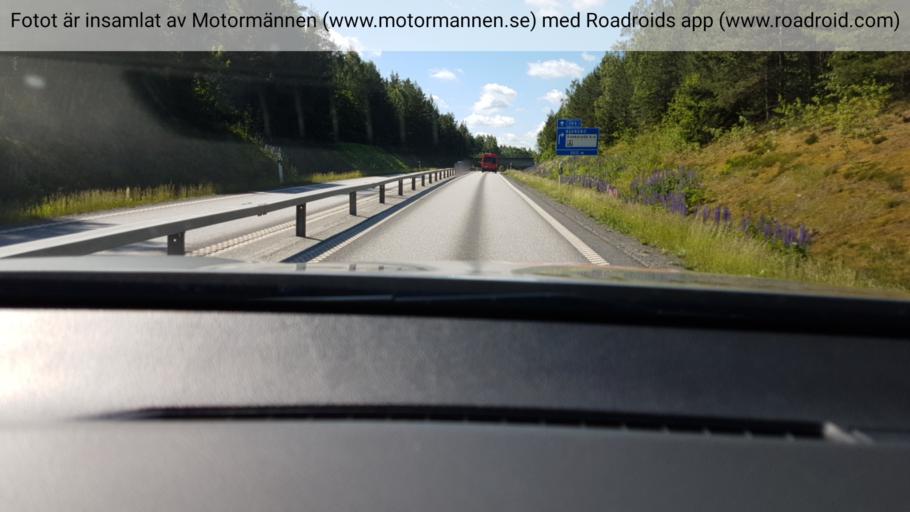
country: SE
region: Joenkoeping
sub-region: Jonkopings Kommun
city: Bankeryd
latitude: 57.8576
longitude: 14.1040
